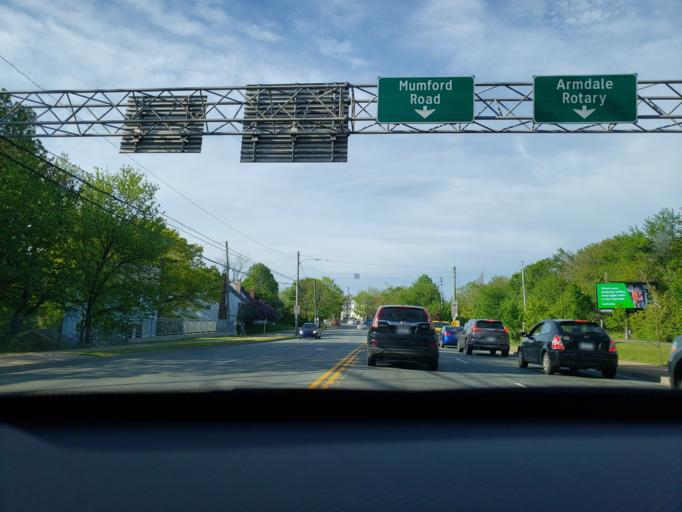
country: CA
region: Nova Scotia
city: Dartmouth
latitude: 44.6516
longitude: -63.6306
